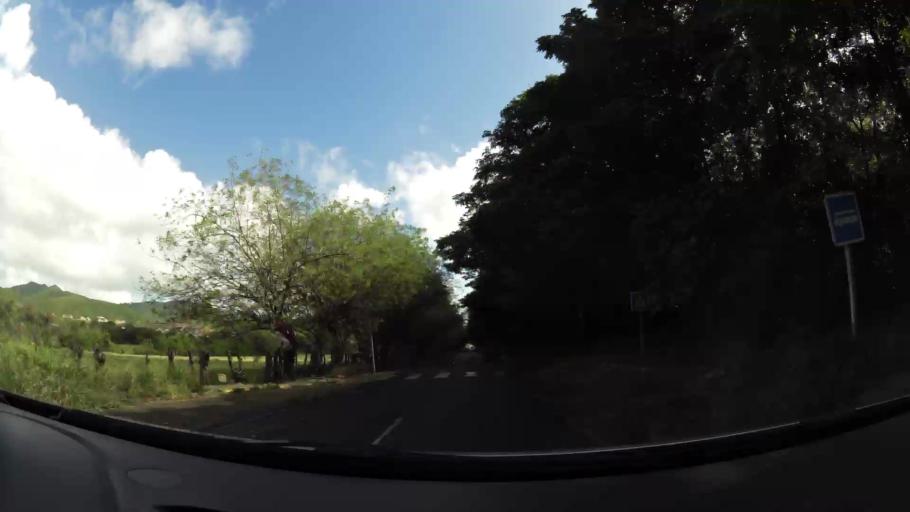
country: MQ
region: Martinique
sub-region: Martinique
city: Les Trois-Ilets
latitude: 14.4772
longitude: -61.0351
